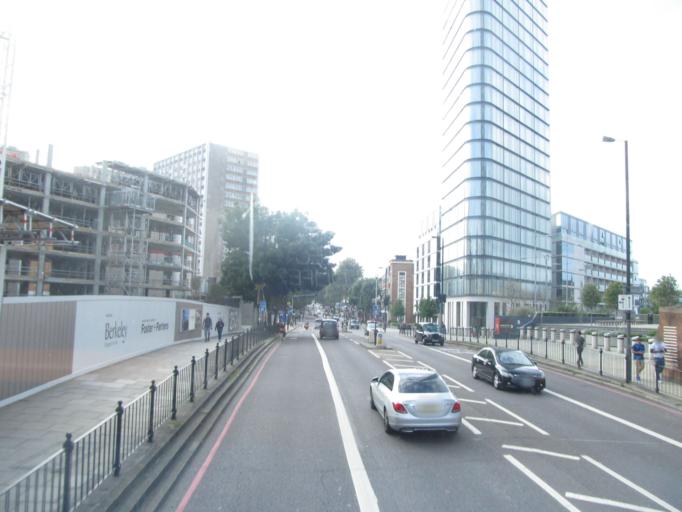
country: GB
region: England
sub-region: Greater London
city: Barbican
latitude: 51.5293
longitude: -0.0957
